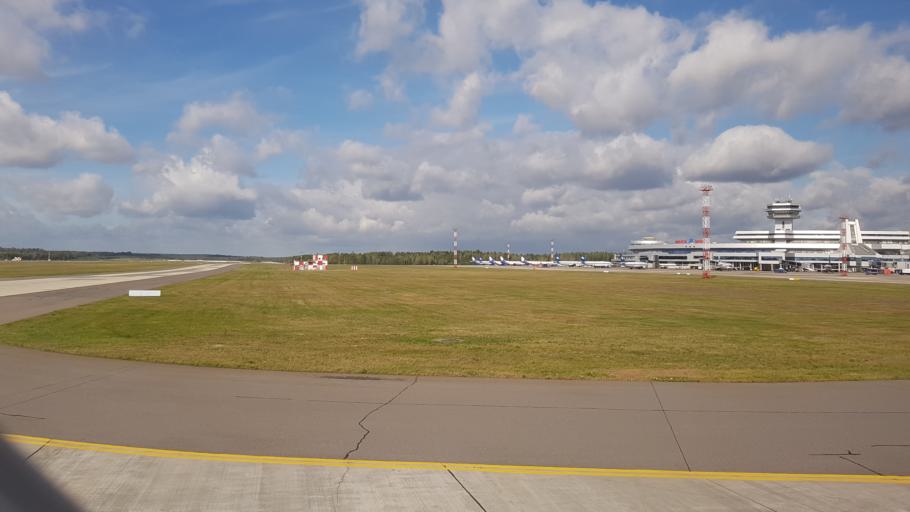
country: BY
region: Minsk
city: Smilavichy
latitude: 53.8840
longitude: 28.0330
